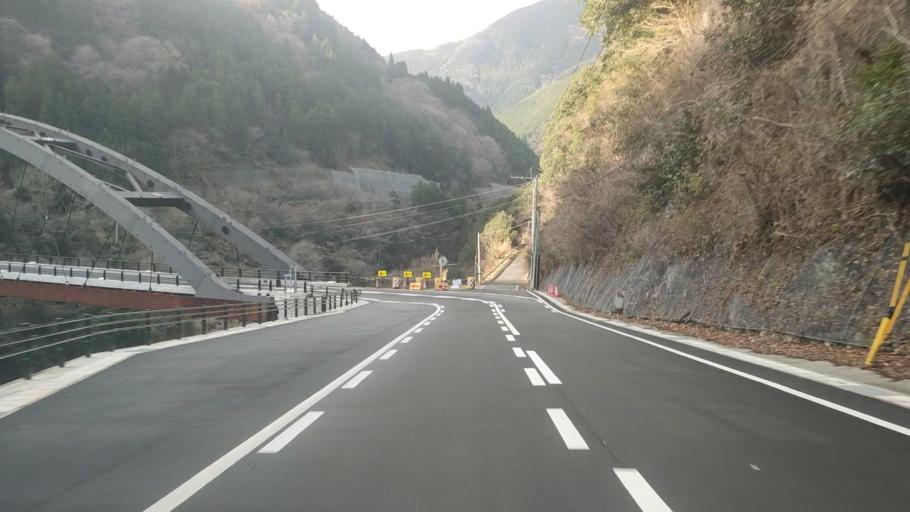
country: JP
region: Kumamoto
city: Hitoyoshi
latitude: 32.4118
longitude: 130.8409
